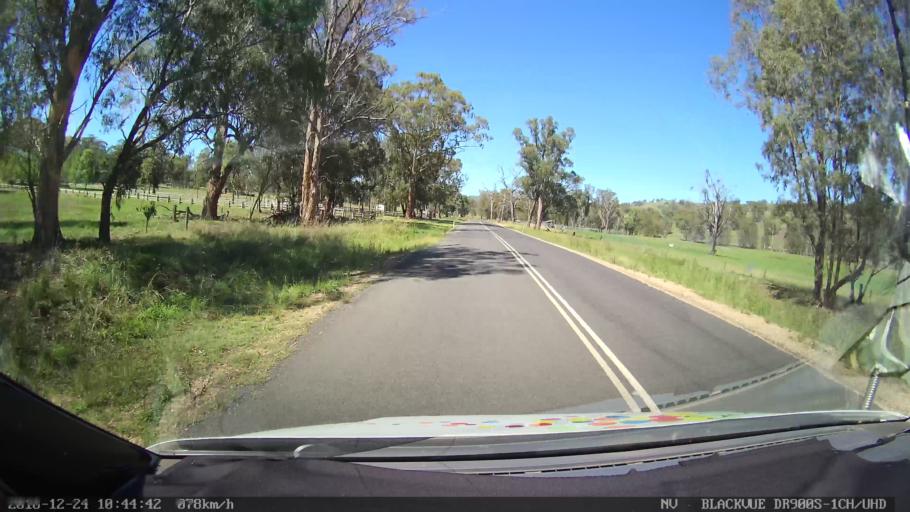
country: AU
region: New South Wales
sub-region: Upper Hunter Shire
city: Merriwa
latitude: -31.8957
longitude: 150.4419
